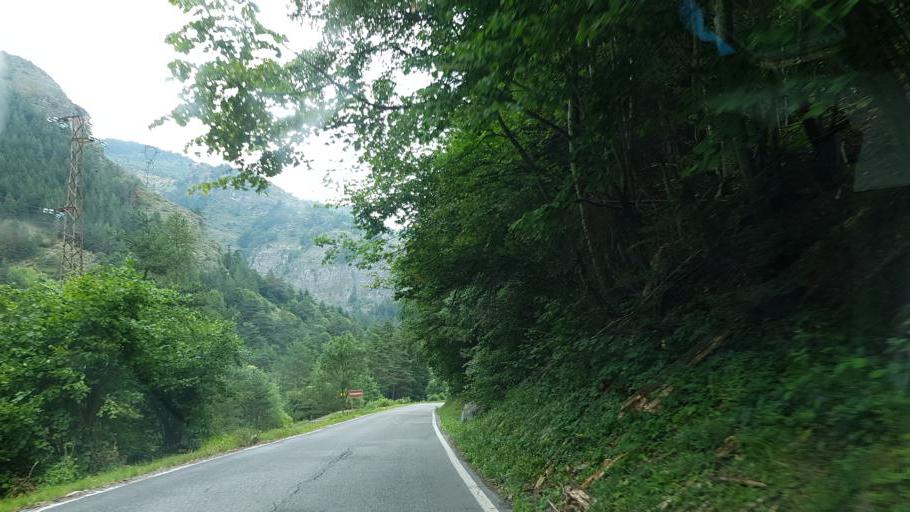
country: IT
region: Piedmont
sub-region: Provincia di Cuneo
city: Marmora
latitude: 44.4915
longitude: 7.0954
